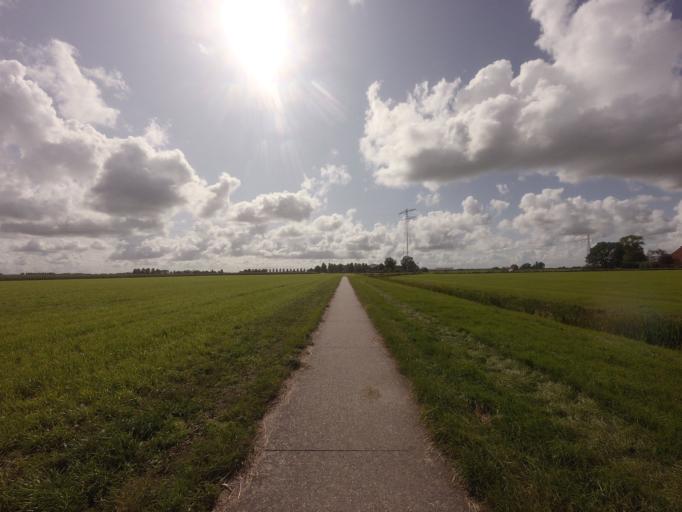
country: NL
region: Friesland
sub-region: Sudwest Fryslan
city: Sneek
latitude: 53.0638
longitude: 5.6346
